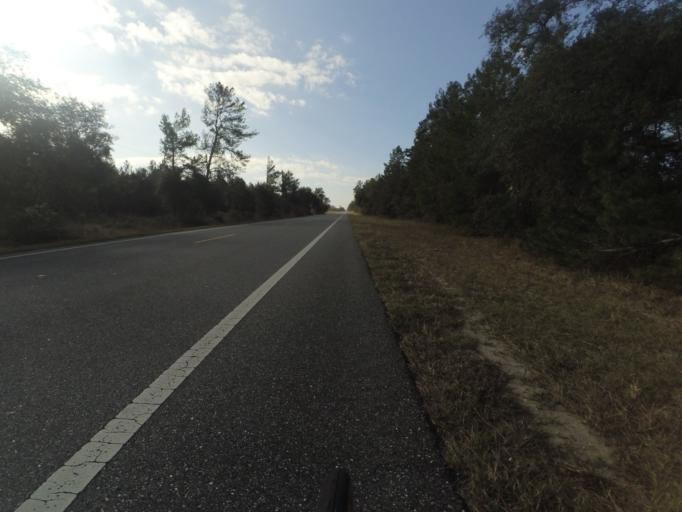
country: US
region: Florida
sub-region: Lake County
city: Astor
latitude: 29.1043
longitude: -81.6188
